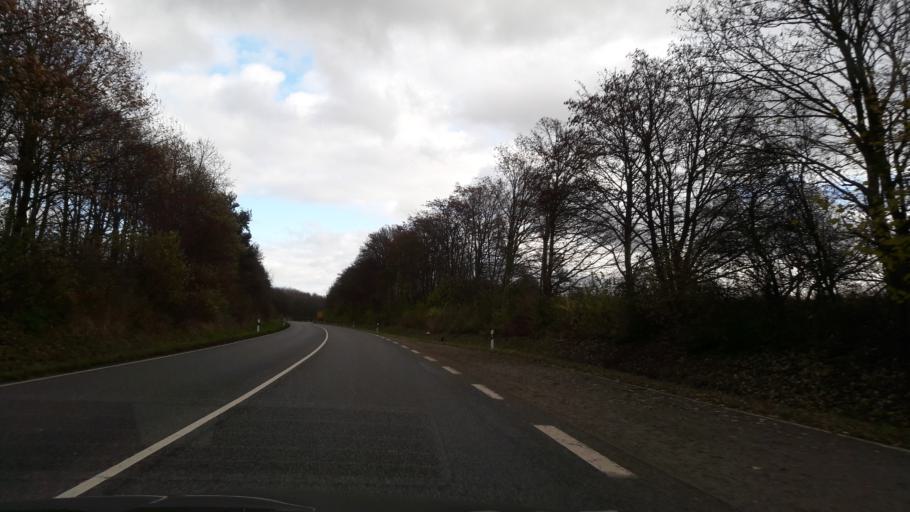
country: DE
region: Rheinland-Pfalz
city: Thomm
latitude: 49.7420
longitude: 6.7888
